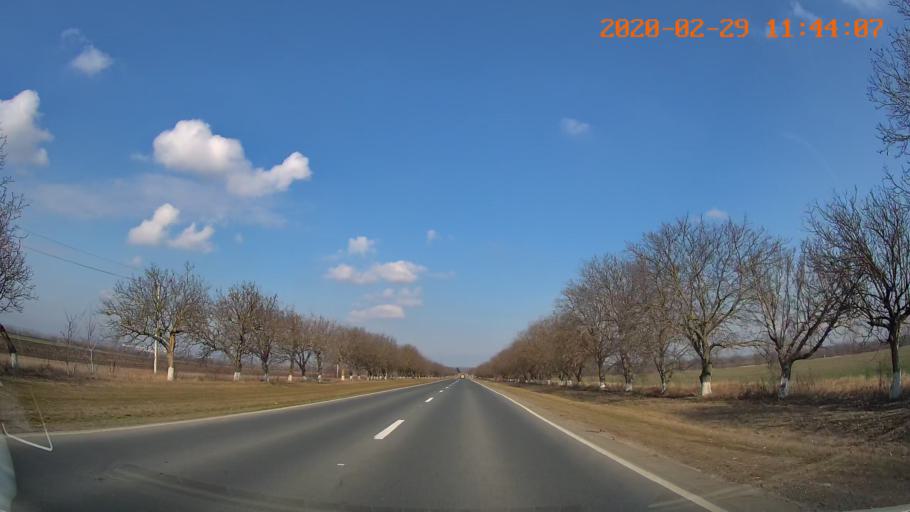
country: MD
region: Rezina
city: Saharna
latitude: 47.7064
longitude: 29.0010
